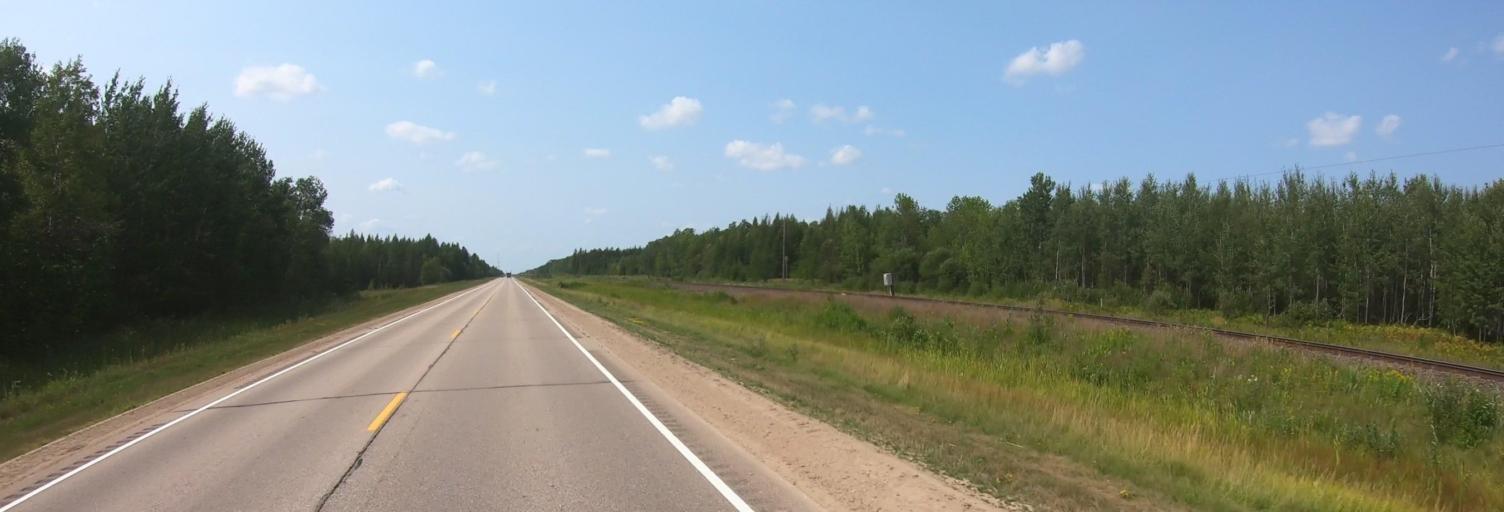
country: US
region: Minnesota
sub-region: Roseau County
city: Warroad
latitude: 48.7794
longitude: -95.0068
